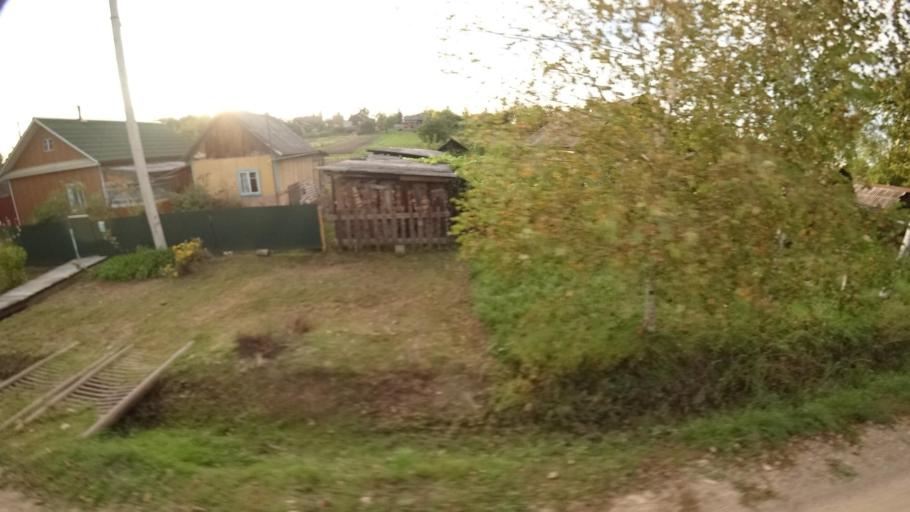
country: RU
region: Primorskiy
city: Yakovlevka
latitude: 44.4250
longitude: 133.4807
